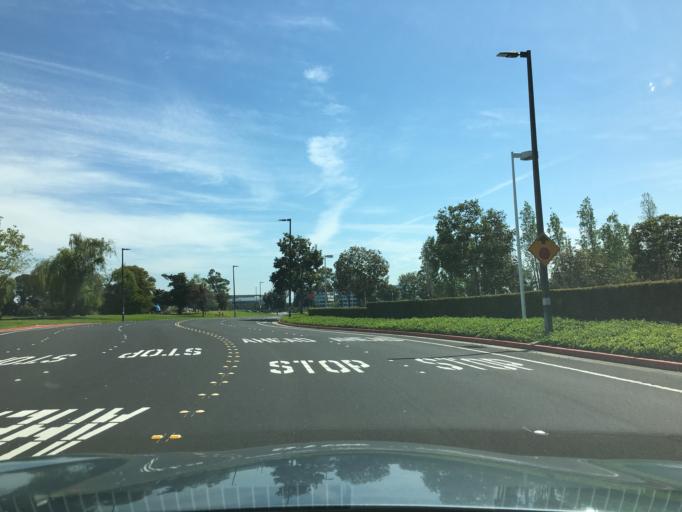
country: US
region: California
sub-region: San Mateo County
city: Redwood Shores
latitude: 37.5306
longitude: -122.2611
